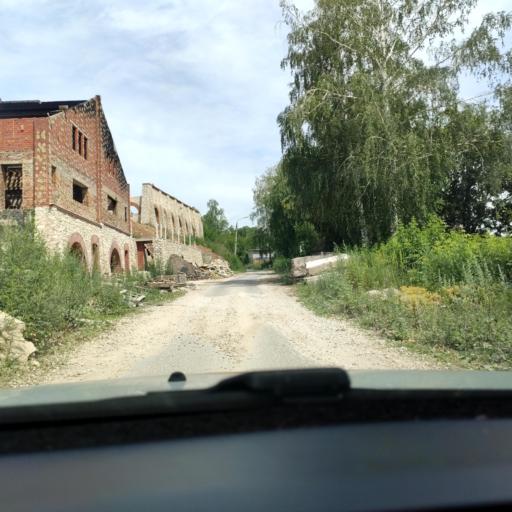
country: RU
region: Samara
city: Volzhskiy
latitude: 53.3407
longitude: 50.2000
